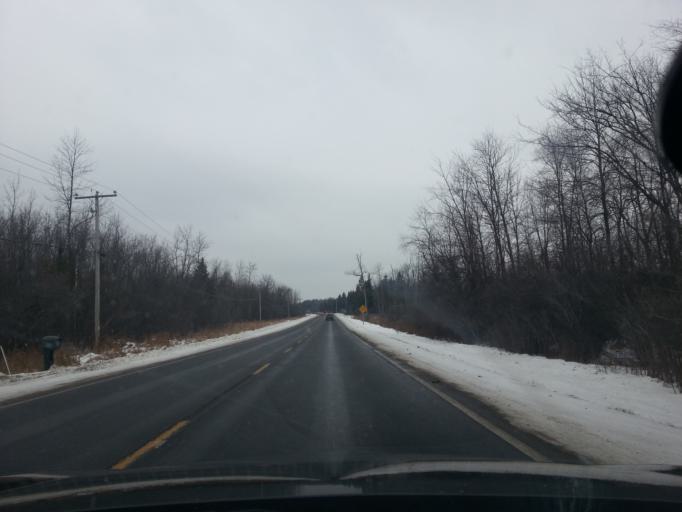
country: CA
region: Ontario
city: Carleton Place
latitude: 45.2954
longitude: -76.0850
